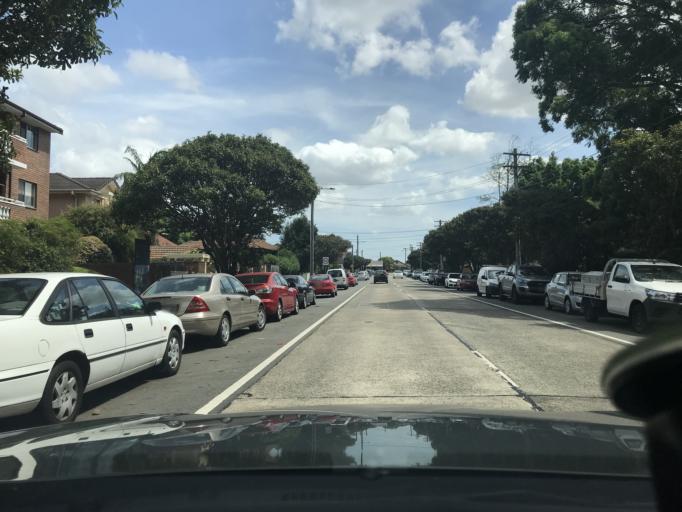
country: AU
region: New South Wales
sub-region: Canada Bay
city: Wareemba
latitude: -33.8552
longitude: 151.1328
